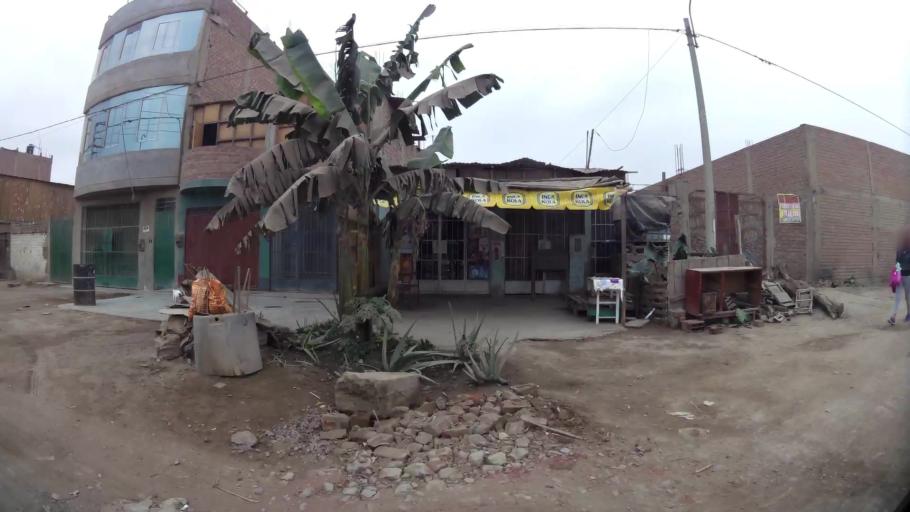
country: PE
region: Lima
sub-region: Lima
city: Independencia
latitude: -11.9550
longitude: -77.0901
